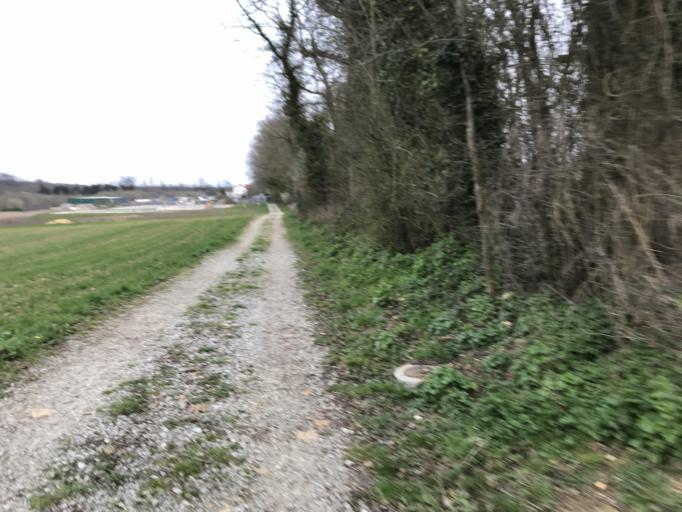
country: FR
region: Ile-de-France
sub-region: Departement de l'Essonne
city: Limours
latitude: 48.6478
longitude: 2.0548
